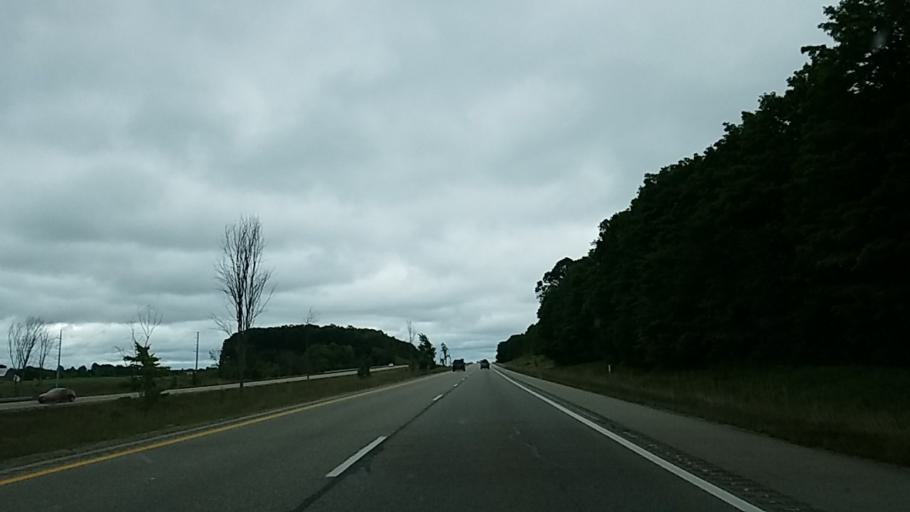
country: US
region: Michigan
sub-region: Otsego County
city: Gaylord
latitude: 45.0681
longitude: -84.6893
